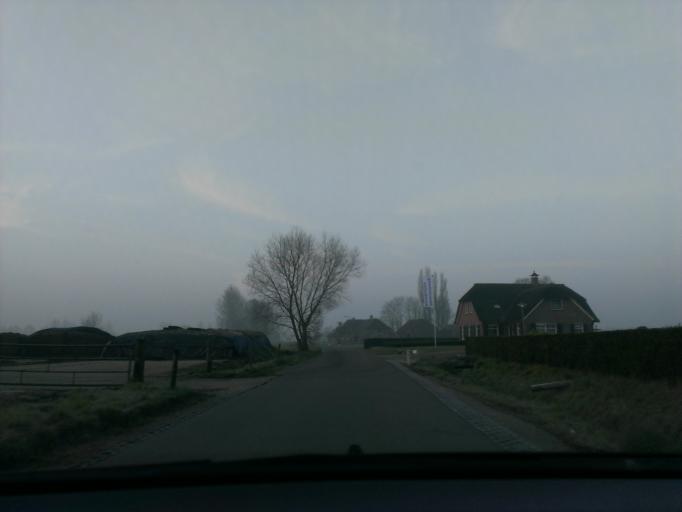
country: NL
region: Gelderland
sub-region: Gemeente Epe
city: Oene
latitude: 52.3399
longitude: 6.0449
